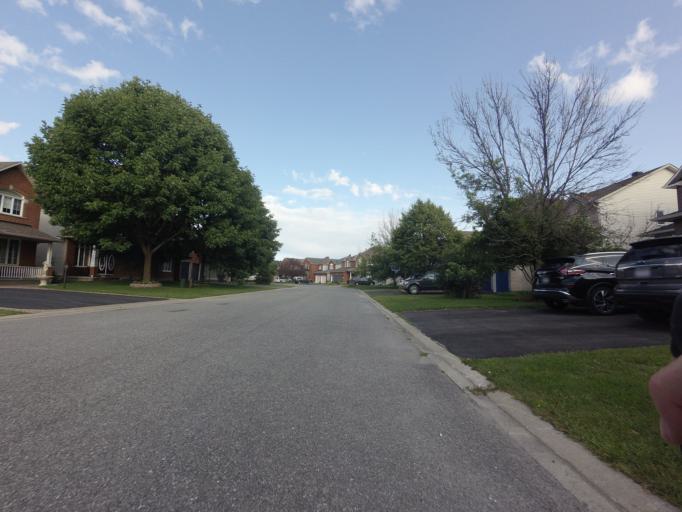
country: CA
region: Ontario
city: Bells Corners
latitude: 45.2891
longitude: -75.7206
